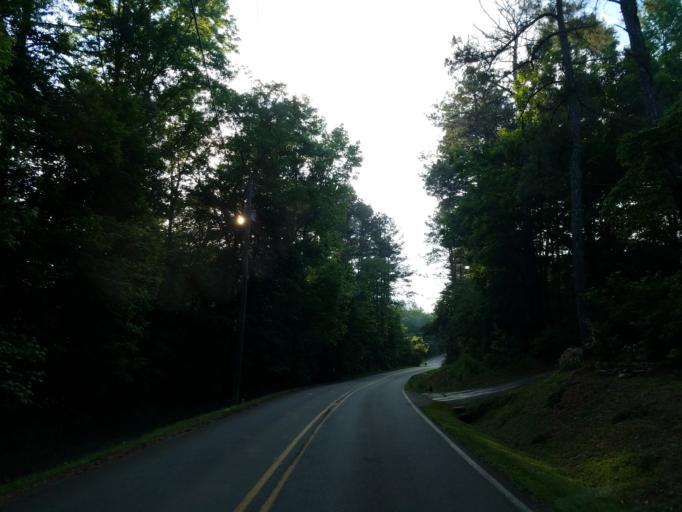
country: US
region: Georgia
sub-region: Cherokee County
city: Ball Ground
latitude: 34.3005
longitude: -84.3857
